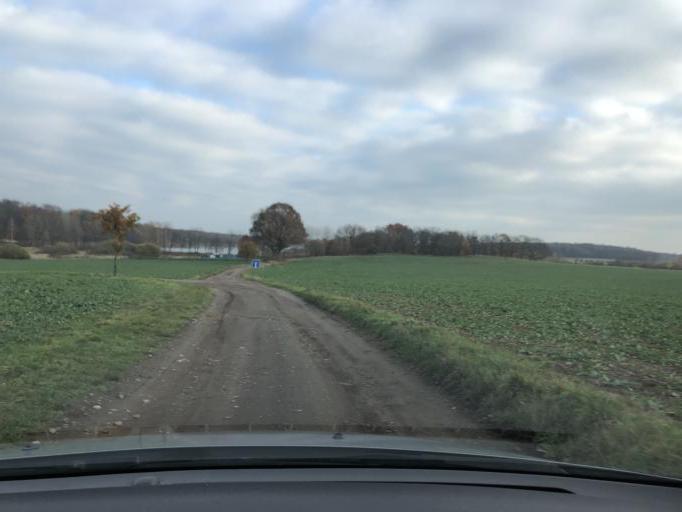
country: DE
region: Saxony
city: Mutzschen
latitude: 51.2787
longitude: 12.8951
